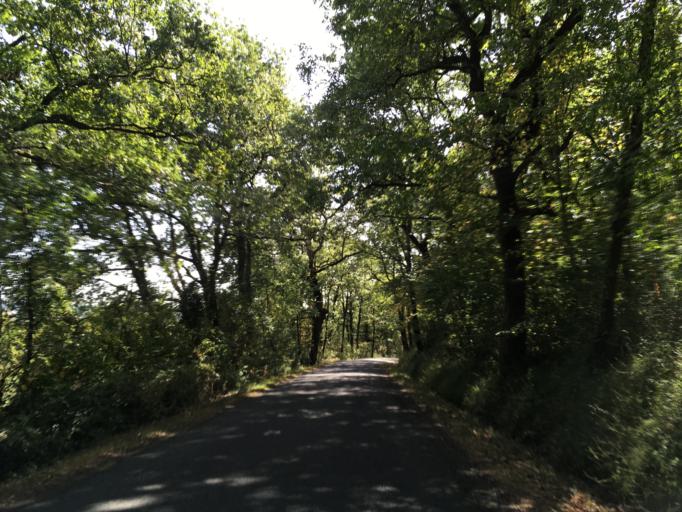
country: FR
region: Midi-Pyrenees
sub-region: Departement du Tarn
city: Lagarrigue
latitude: 43.5934
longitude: 2.3127
